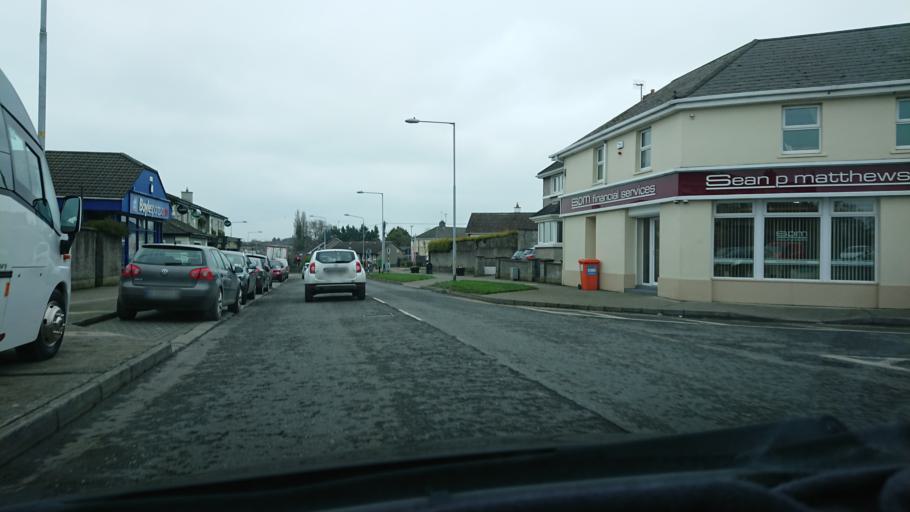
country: IE
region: Leinster
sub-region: Lu
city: Drogheda
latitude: 53.7196
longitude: -6.3418
